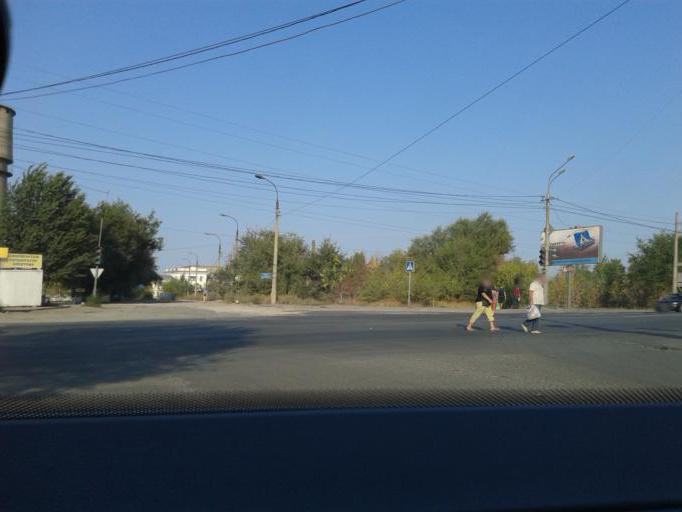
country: RU
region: Volgograd
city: Gorodishche
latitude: 48.7674
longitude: 44.4737
